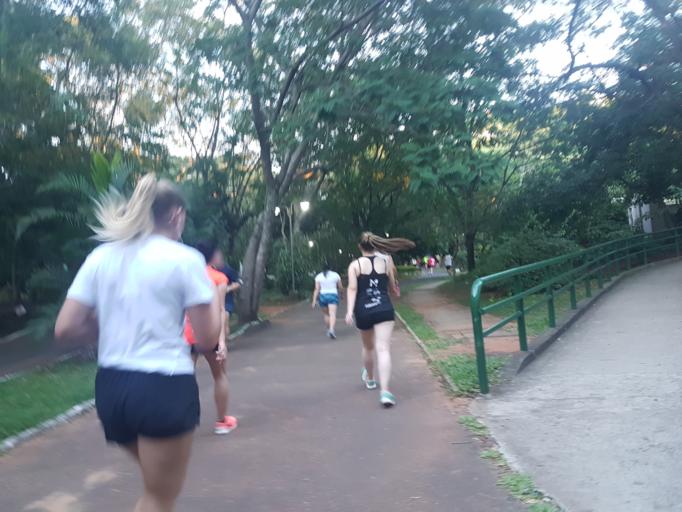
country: PY
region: Asuncion
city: Asuncion
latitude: -25.2765
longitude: -57.5783
